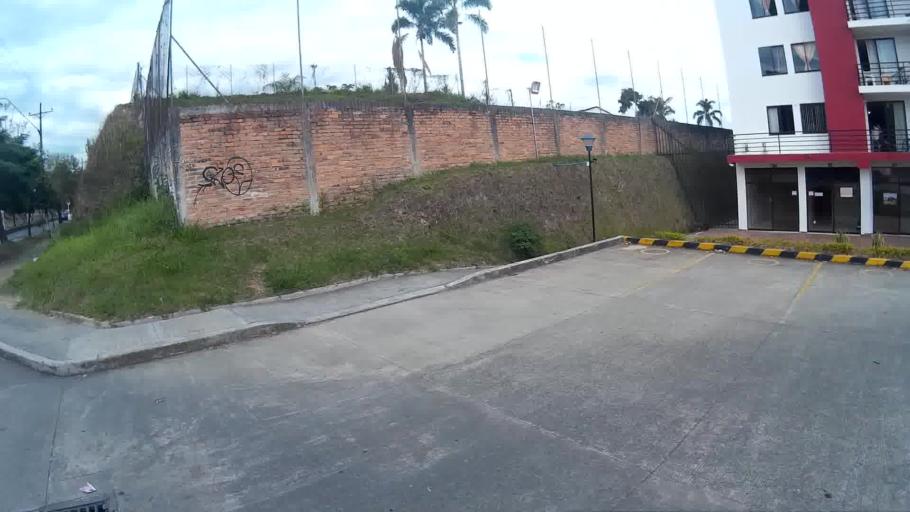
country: CO
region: Risaralda
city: Pereira
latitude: 4.8116
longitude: -75.7378
